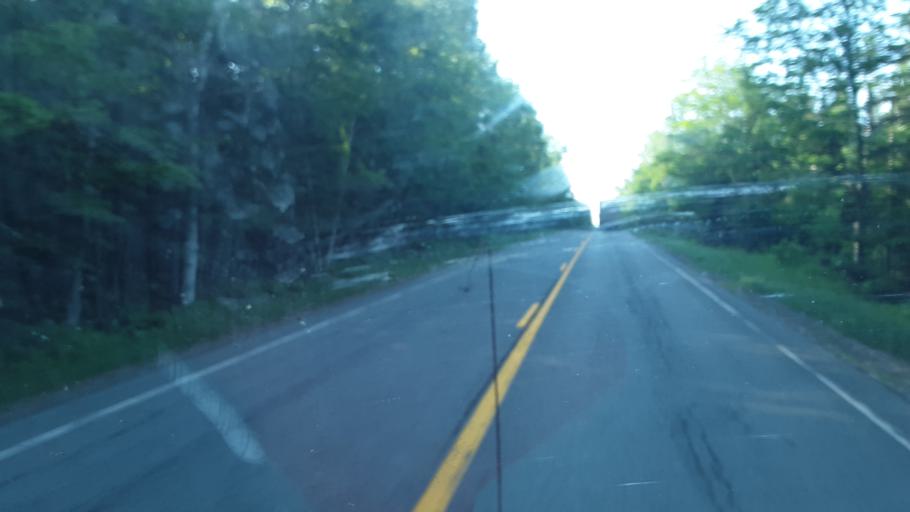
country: US
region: Maine
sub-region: Penobscot County
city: Patten
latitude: 46.1918
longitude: -68.2594
